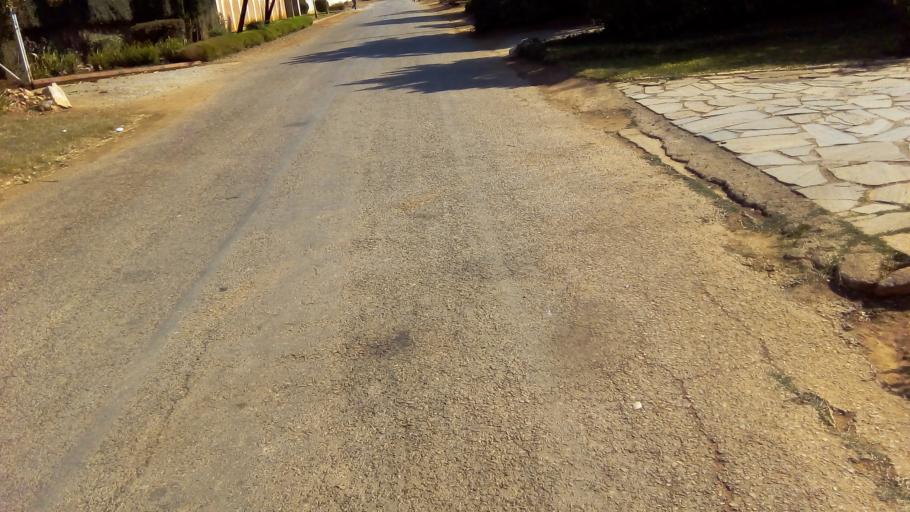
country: ZM
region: Lusaka
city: Lusaka
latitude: -15.4431
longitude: 28.3492
